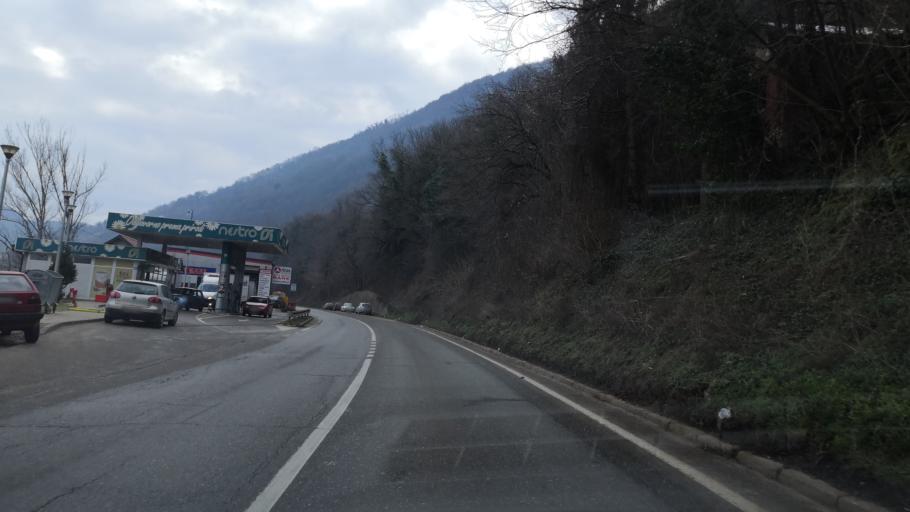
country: RS
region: Central Serbia
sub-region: Macvanski Okrug
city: Mali Zvornik
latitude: 44.3719
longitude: 19.1013
